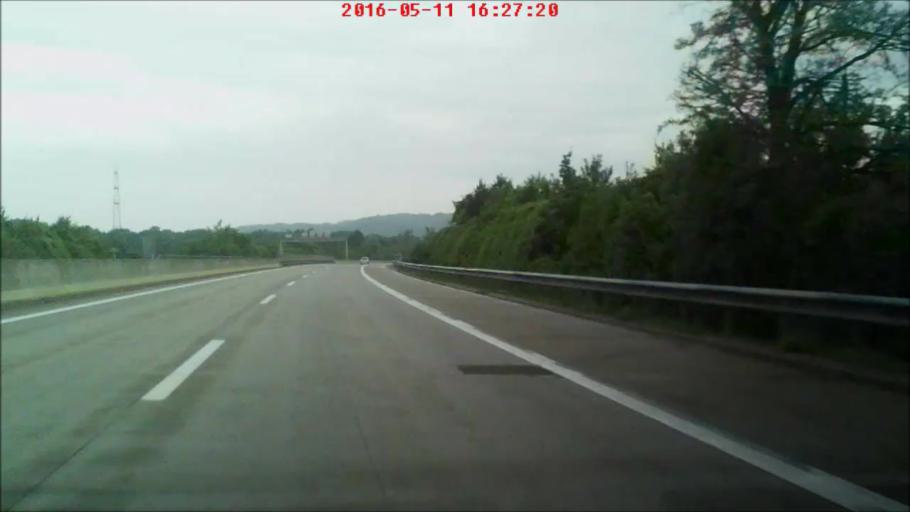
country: AT
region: Styria
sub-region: Politischer Bezirk Leibnitz
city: Strass in Steiermark
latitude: 46.7263
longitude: 15.6464
